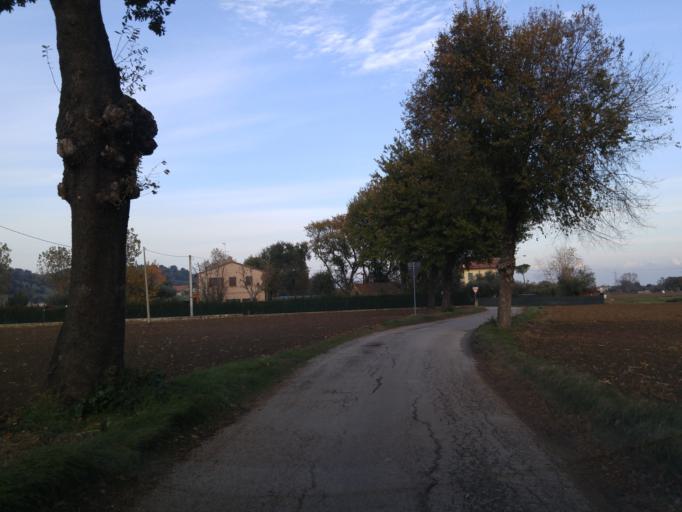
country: IT
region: The Marches
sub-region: Provincia di Pesaro e Urbino
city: Cuccurano
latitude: 43.7910
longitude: 12.9601
